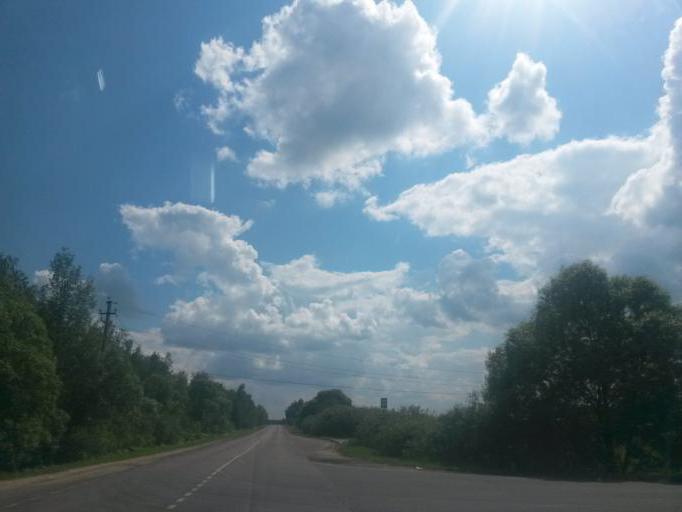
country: RU
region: Moskovskaya
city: Belyye Stolby
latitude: 55.2815
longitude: 37.7736
